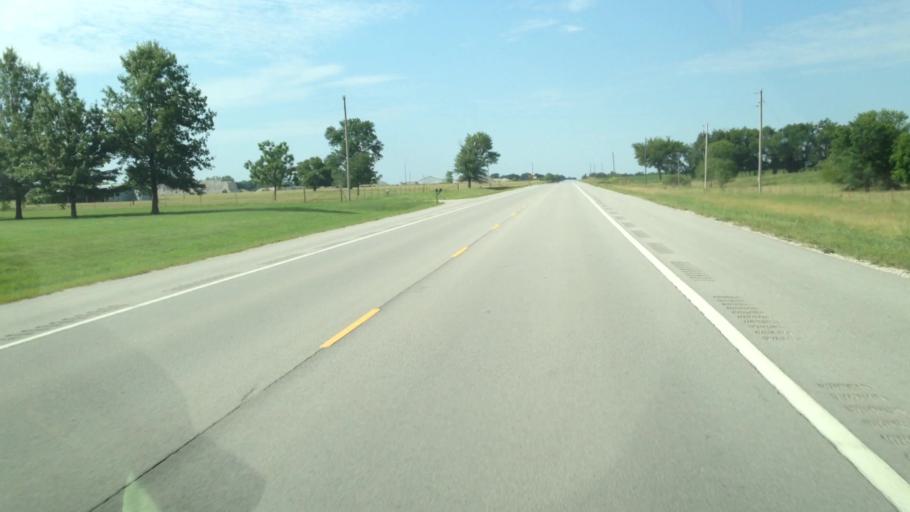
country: US
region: Kansas
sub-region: Labette County
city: Parsons
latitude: 37.2752
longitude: -95.2673
